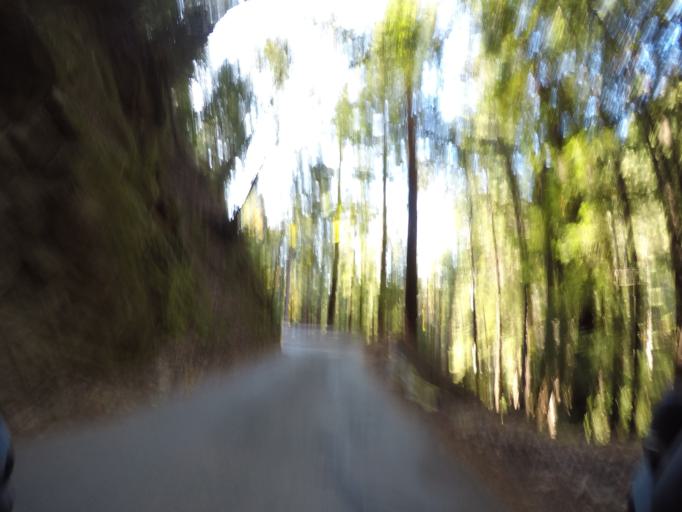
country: US
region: California
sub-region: Santa Clara County
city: Lexington Hills
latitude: 37.1503
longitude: -122.0152
